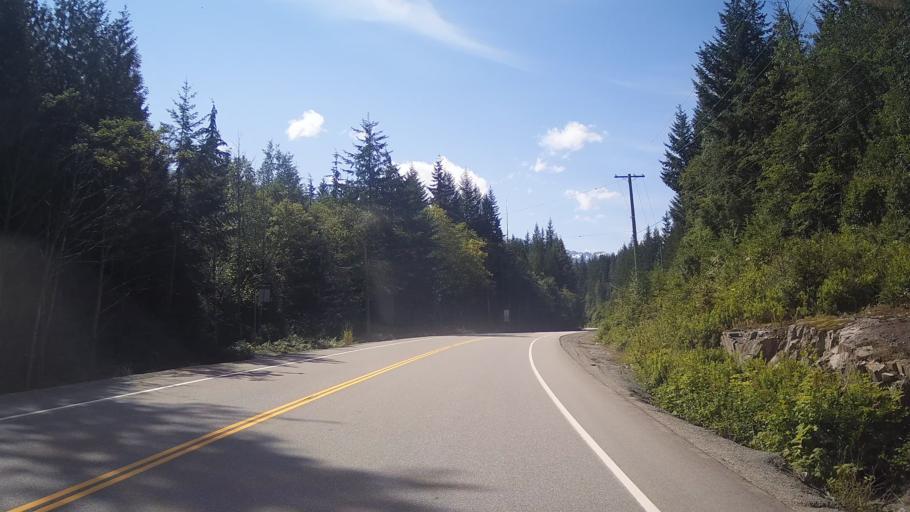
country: CA
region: British Columbia
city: Whistler
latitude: 50.2003
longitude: -122.8805
